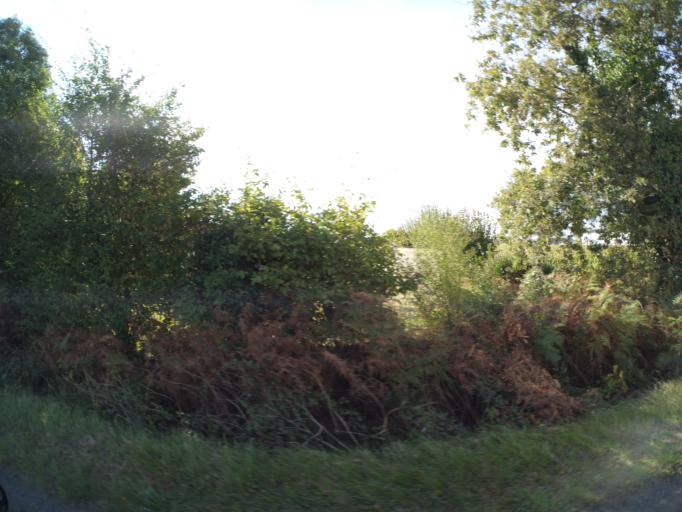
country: FR
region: Pays de la Loire
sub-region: Departement de la Loire-Atlantique
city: Mouzillon
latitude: 47.1260
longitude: -1.2764
